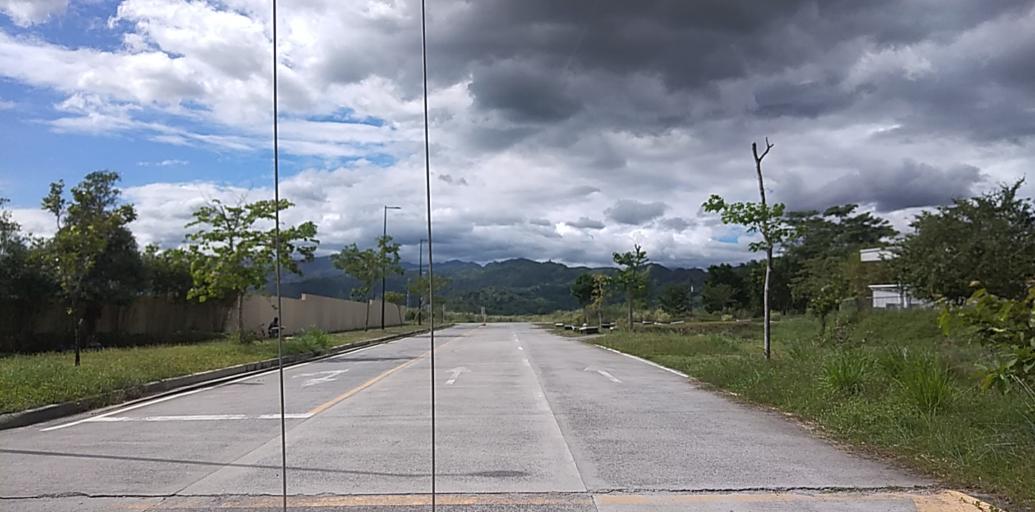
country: PH
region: Central Luzon
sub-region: Province of Pampanga
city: Dolores
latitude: 15.1159
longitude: 120.5134
